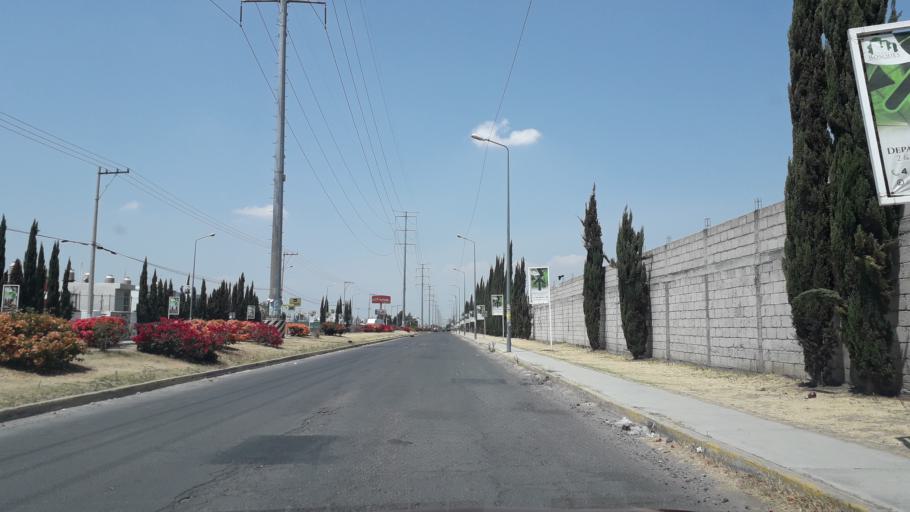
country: MX
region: Puebla
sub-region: Amozoc
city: Casa Blanca
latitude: 19.0617
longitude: -98.1229
